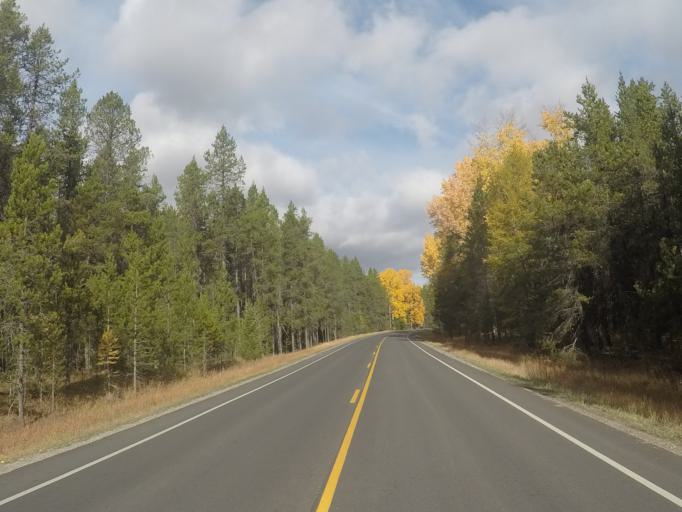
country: US
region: Montana
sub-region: Flathead County
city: Columbia Falls
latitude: 48.5163
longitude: -113.9895
